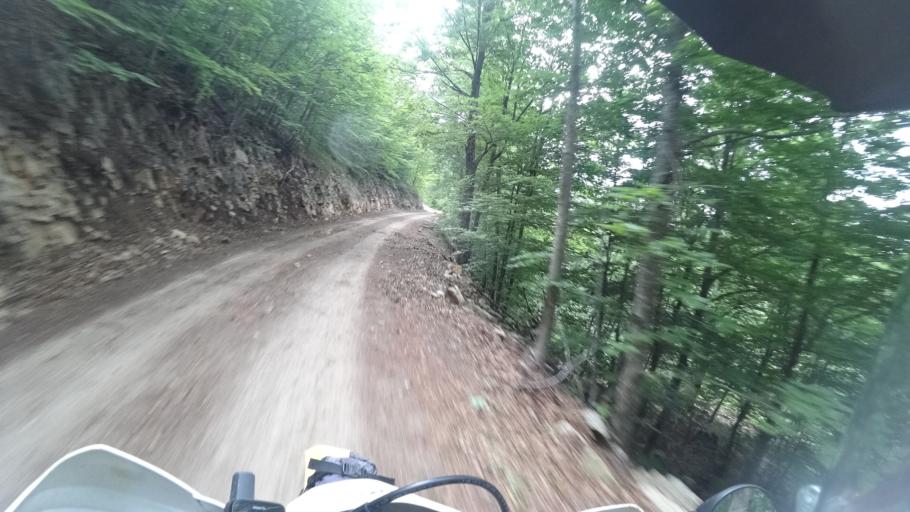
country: HR
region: Zadarska
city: Obrovac
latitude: 44.2801
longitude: 15.7055
